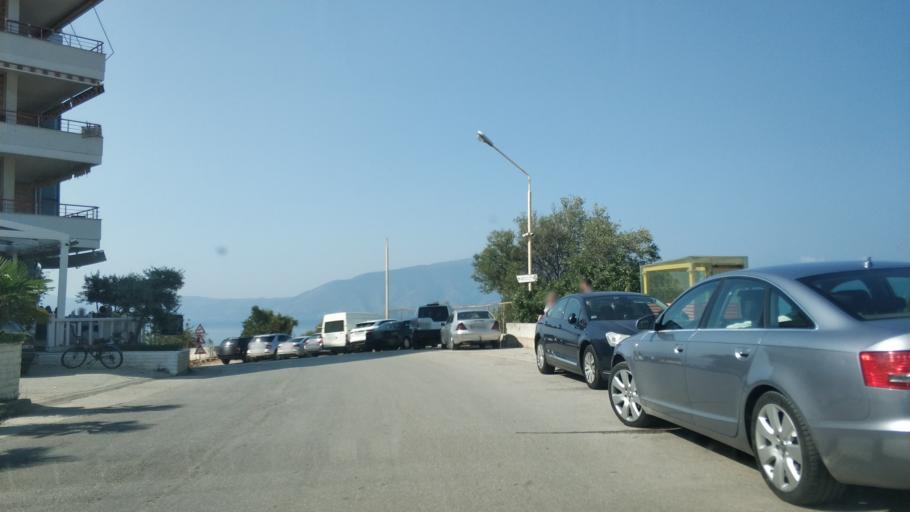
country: AL
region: Vlore
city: Vlore
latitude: 40.4146
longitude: 19.4815
